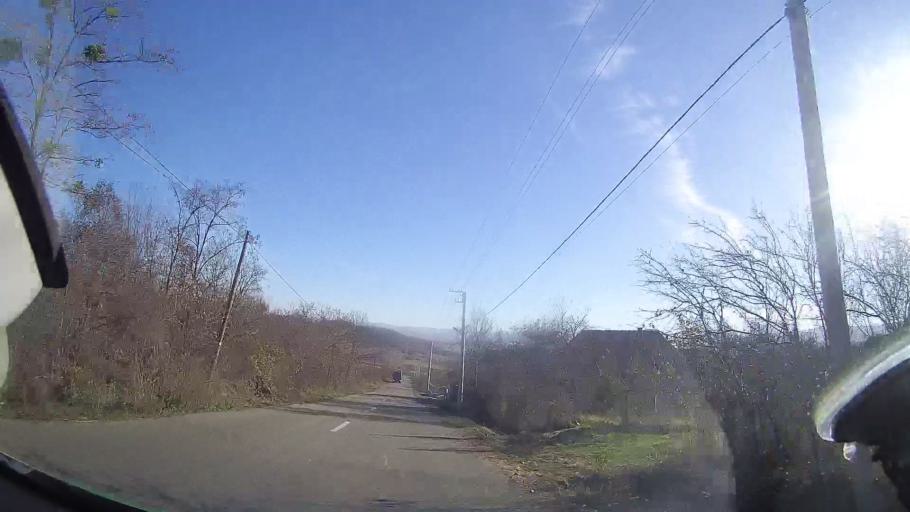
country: RO
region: Bihor
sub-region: Comuna Vadu Crisului
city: Vadu Crisului
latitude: 46.9732
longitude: 22.5415
